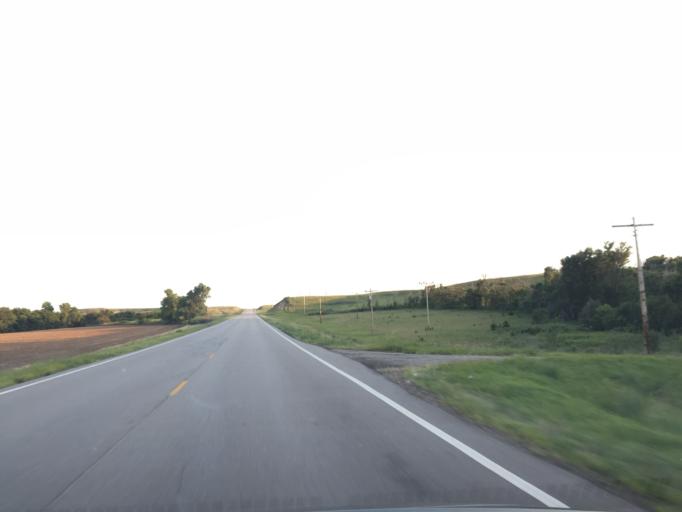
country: US
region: Kansas
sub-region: Ellsworth County
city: Ellsworth
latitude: 38.6205
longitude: -98.2018
